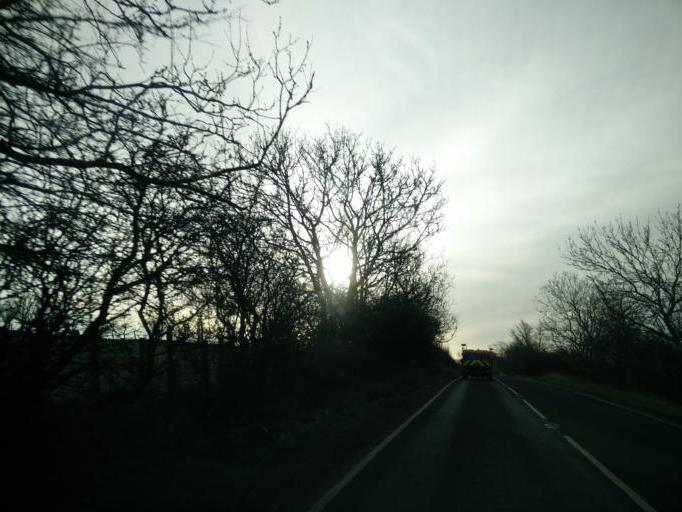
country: GB
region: England
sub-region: County Durham
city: Crook
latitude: 54.6755
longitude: -1.7146
